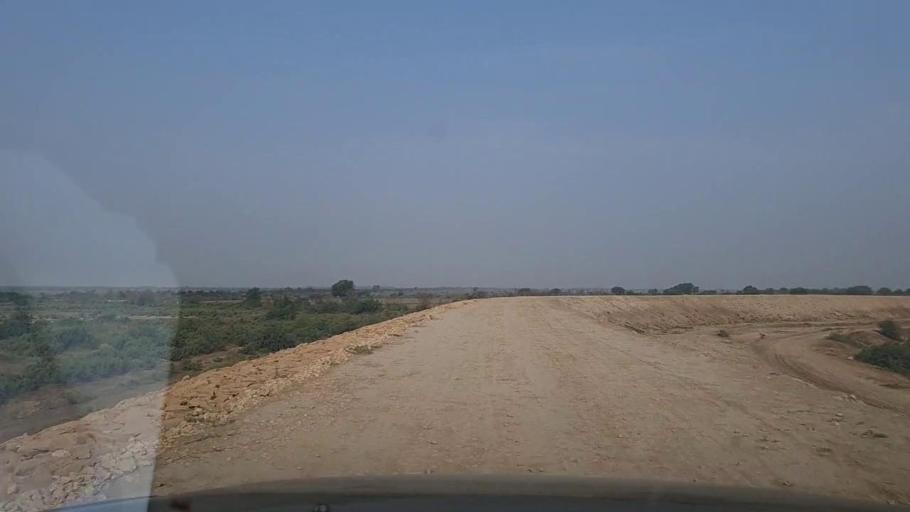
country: PK
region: Sindh
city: Bulri
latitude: 24.9672
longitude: 68.2904
